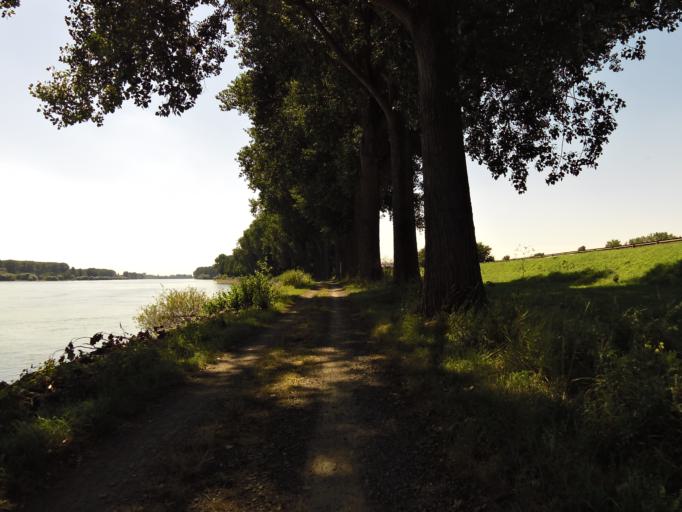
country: DE
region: Rheinland-Pfalz
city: Bodenheim
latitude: 49.9420
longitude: 8.3399
